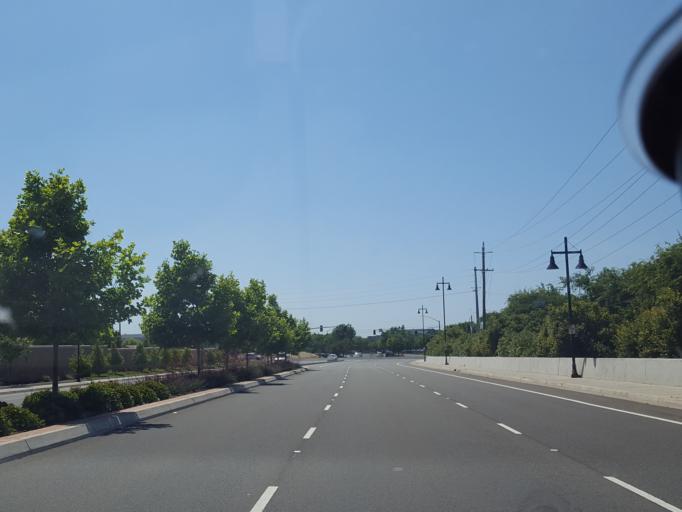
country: US
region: California
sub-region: Sacramento County
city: Rancho Cordova
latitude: 38.5846
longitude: -121.2678
